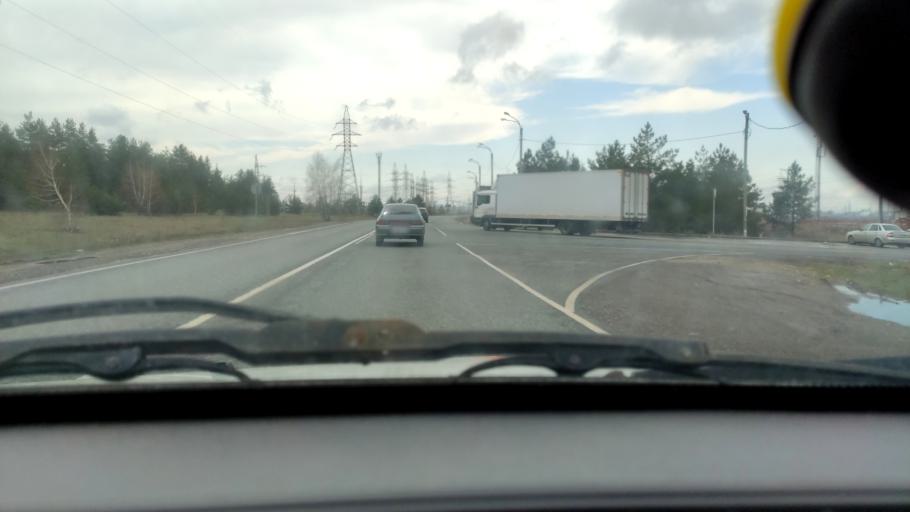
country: RU
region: Samara
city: Zhigulevsk
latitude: 53.5651
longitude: 49.5461
